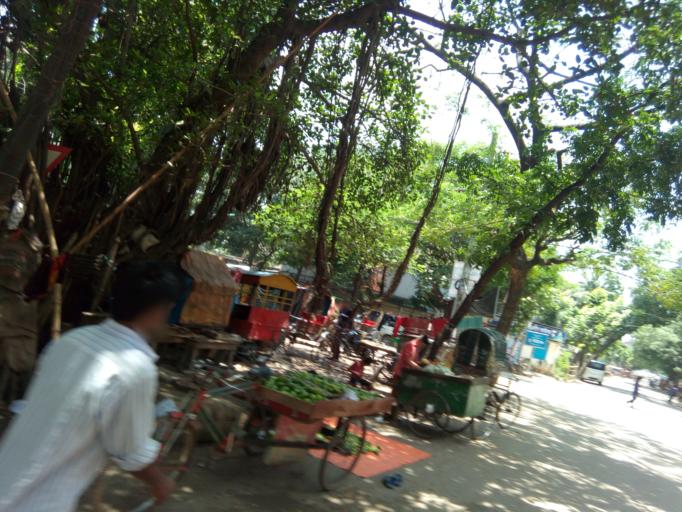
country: BD
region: Dhaka
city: Paltan
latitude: 23.7609
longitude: 90.4012
